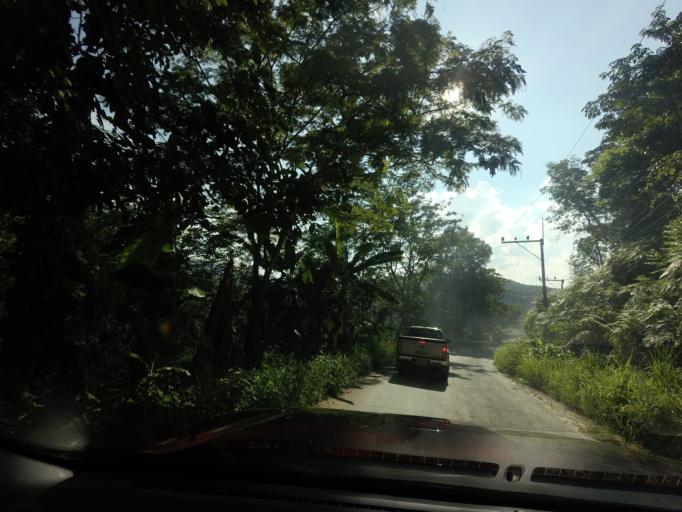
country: TH
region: Yala
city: Than To
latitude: 6.0811
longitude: 101.3282
